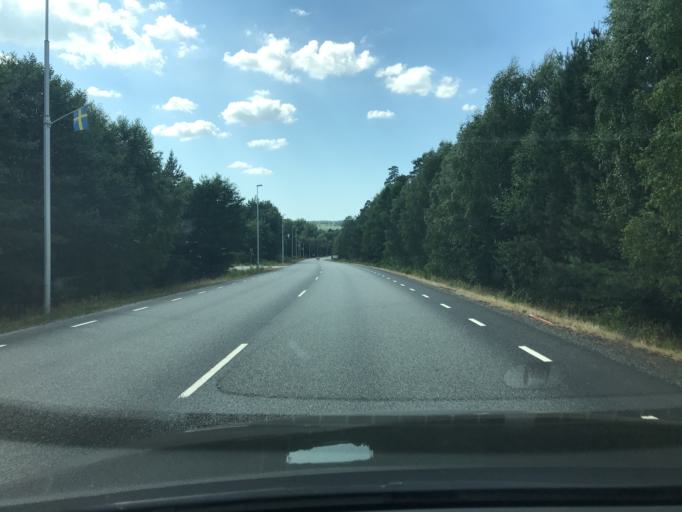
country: SE
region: Skane
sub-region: Hassleholms Kommun
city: Hastveda
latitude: 56.2760
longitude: 13.9446
